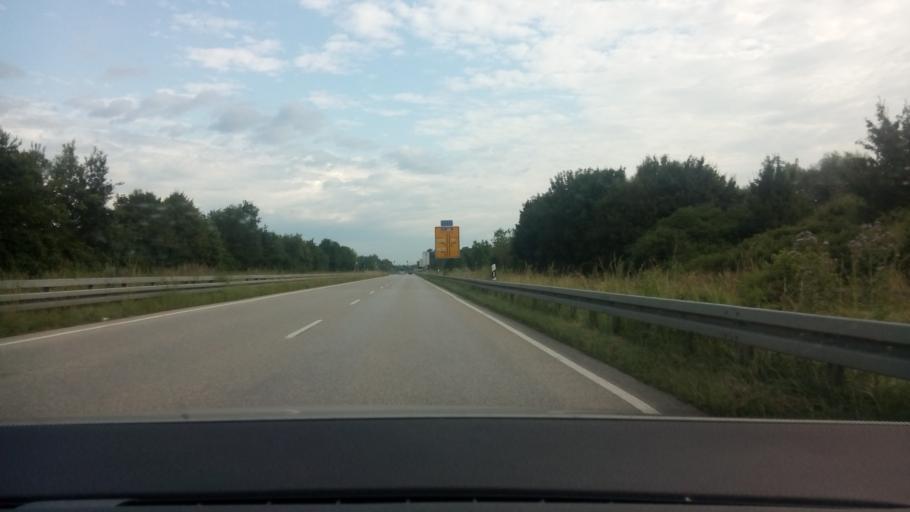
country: DE
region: Bavaria
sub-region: Upper Bavaria
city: Unterschleissheim
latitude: 48.2608
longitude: 11.5971
